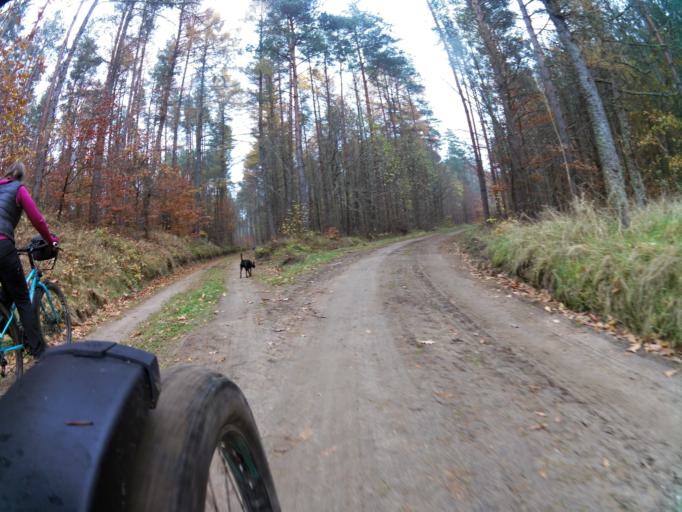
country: PL
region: Pomeranian Voivodeship
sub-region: Powiat wejherowski
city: Orle
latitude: 54.6914
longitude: 18.1553
